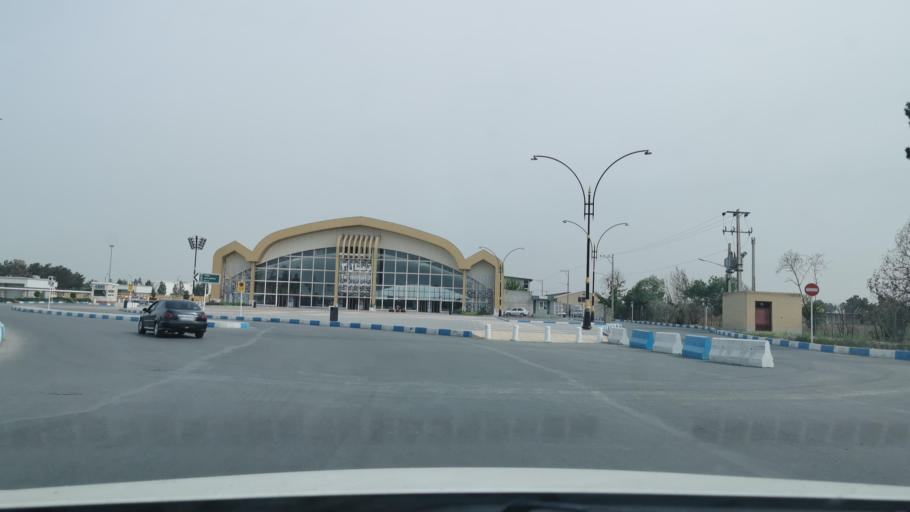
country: IR
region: Razavi Khorasan
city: Mashhad
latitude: 36.2256
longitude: 59.6402
